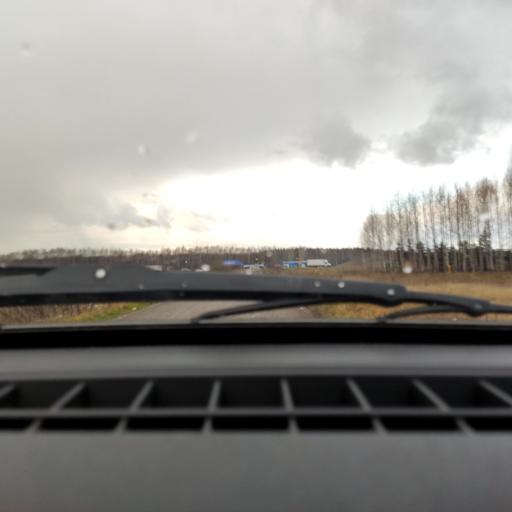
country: RU
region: Bashkortostan
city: Iglino
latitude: 54.7439
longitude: 56.3167
